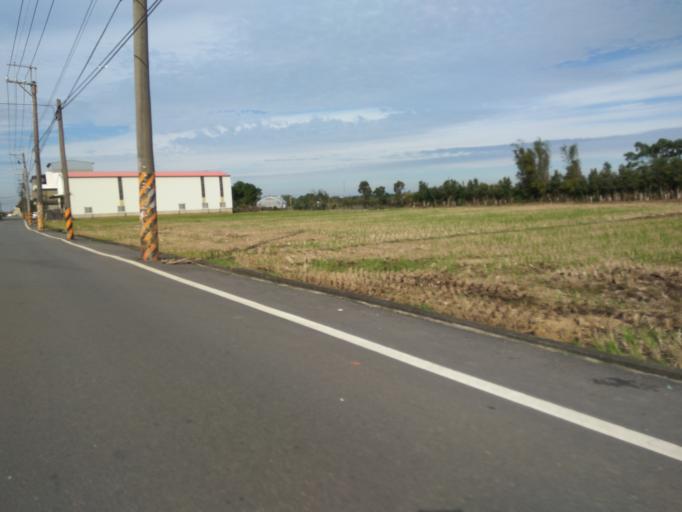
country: TW
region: Taiwan
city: Taoyuan City
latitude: 24.9511
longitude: 121.1340
